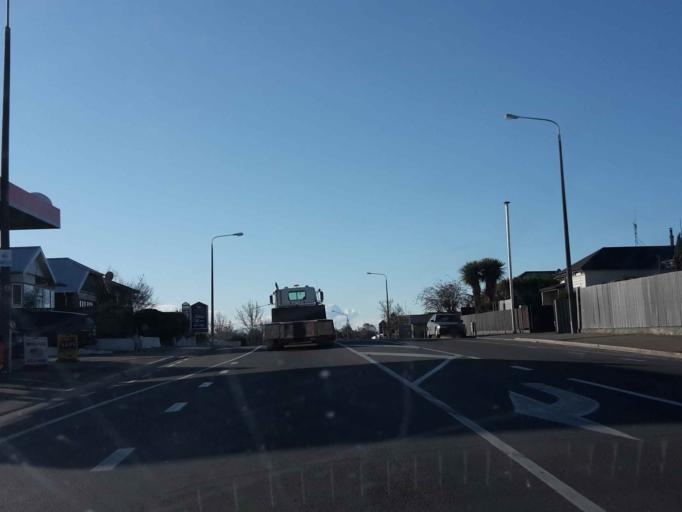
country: NZ
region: Canterbury
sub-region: Timaru District
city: Timaru
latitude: -44.4131
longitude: 171.2483
